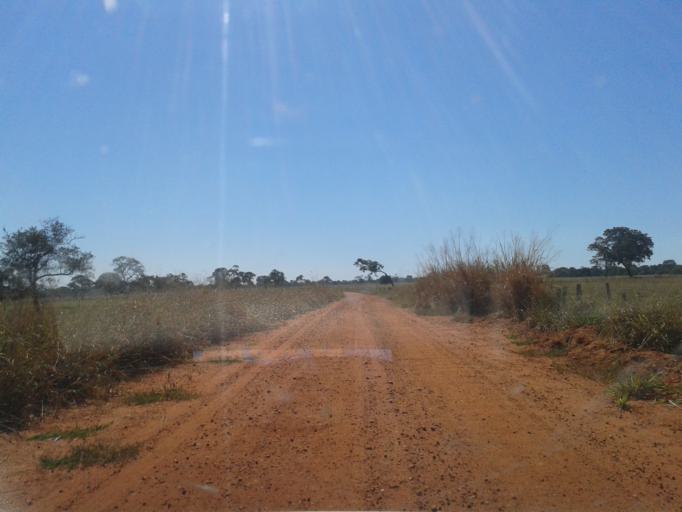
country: BR
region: Minas Gerais
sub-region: Santa Vitoria
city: Santa Vitoria
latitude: -19.0747
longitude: -50.3592
